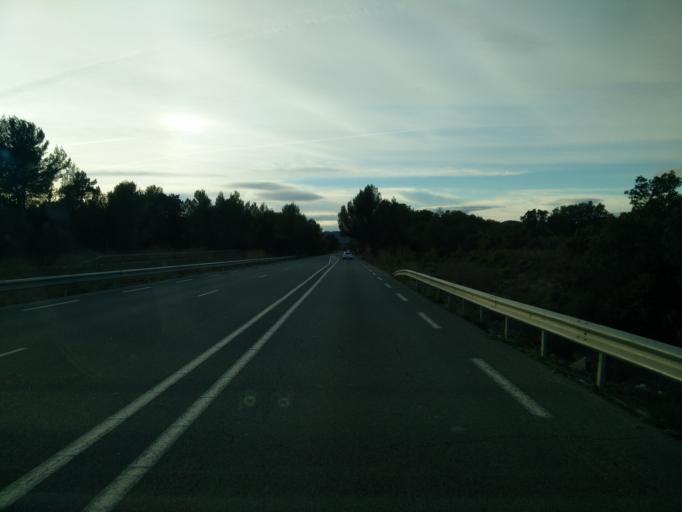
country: FR
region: Provence-Alpes-Cote d'Azur
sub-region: Departement du Var
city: La Londe-les-Maures
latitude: 43.1486
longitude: 6.2752
